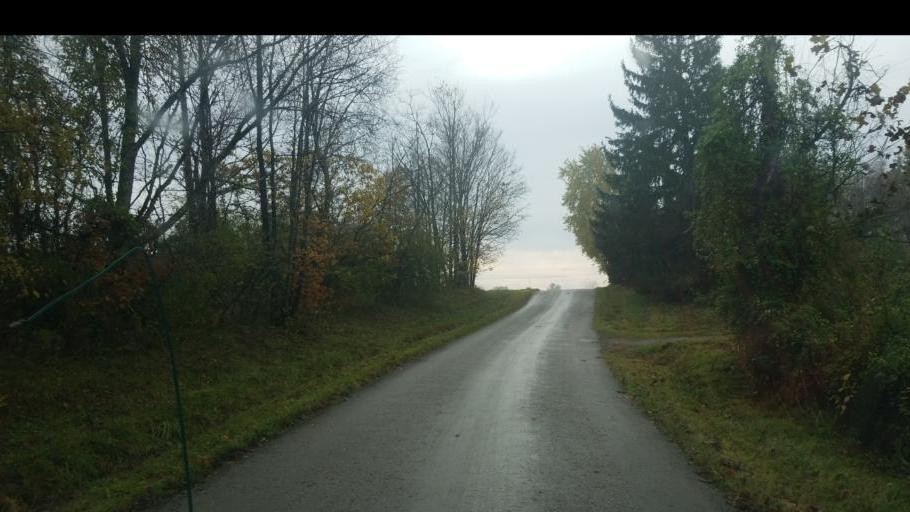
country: US
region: Ohio
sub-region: Morgan County
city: McConnelsville
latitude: 39.4954
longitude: -81.8140
